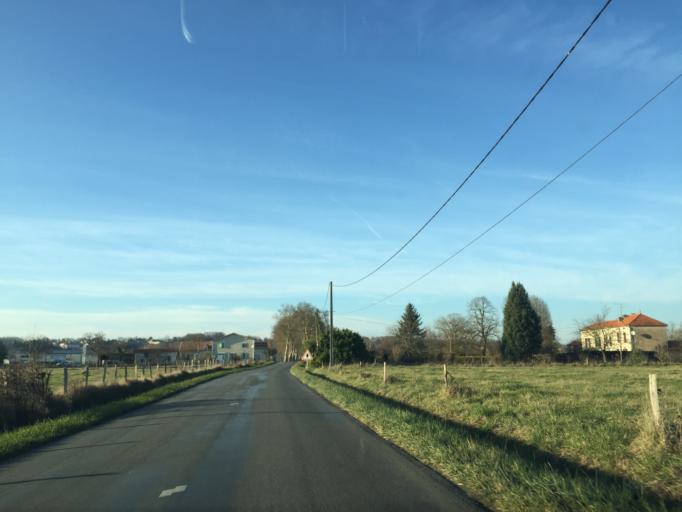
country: FR
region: Aquitaine
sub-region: Departement de la Dordogne
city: Saint-Aulaye
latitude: 45.2635
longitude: 0.1873
